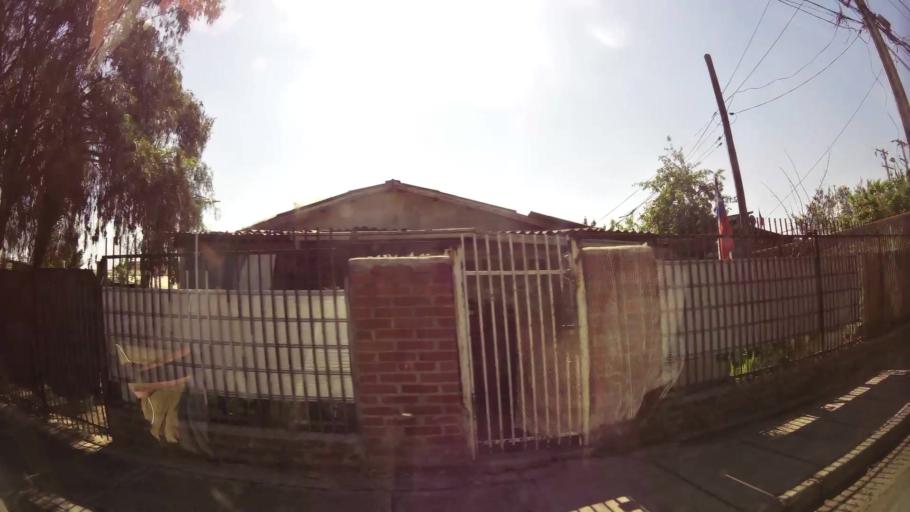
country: CL
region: Santiago Metropolitan
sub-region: Provincia de Talagante
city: Penaflor
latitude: -33.5668
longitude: -70.8028
